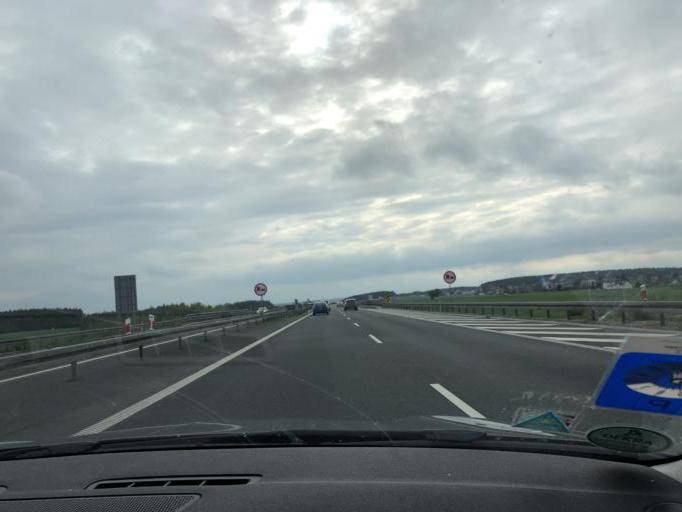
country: PL
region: Opole Voivodeship
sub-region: Powiat krapkowicki
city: Gogolin
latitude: 50.4828
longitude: 18.0300
